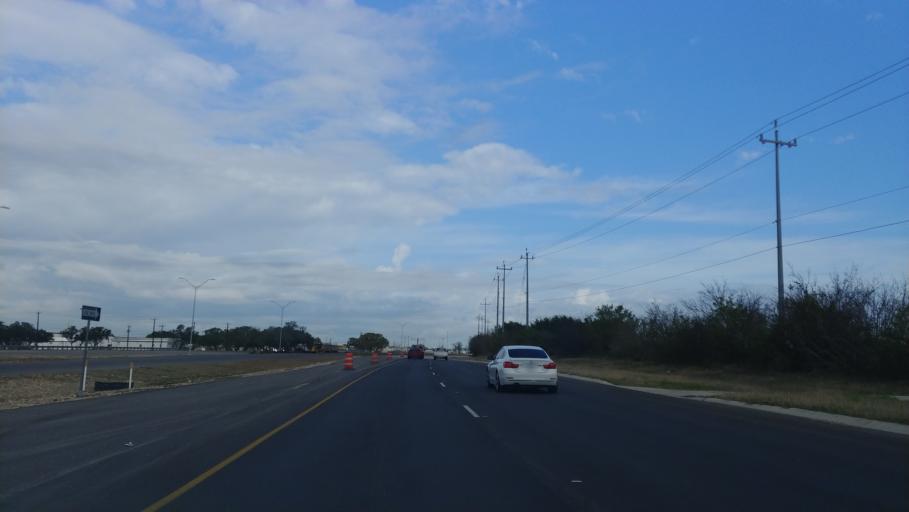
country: US
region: Texas
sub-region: Bexar County
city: Lackland Air Force Base
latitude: 29.4237
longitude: -98.7098
